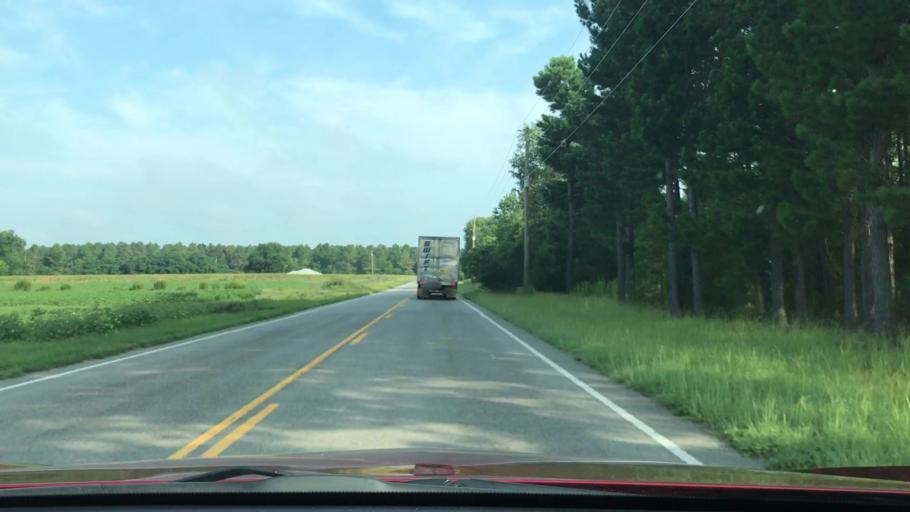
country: US
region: South Carolina
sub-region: Barnwell County
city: Blackville
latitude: 33.5985
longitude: -81.2600
